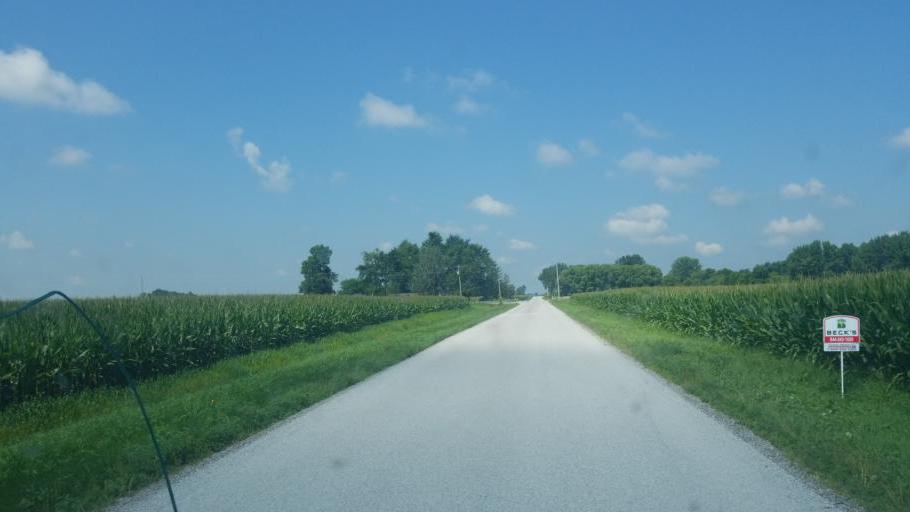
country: US
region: Ohio
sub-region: Hardin County
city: Ada
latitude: 40.6746
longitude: -83.7693
